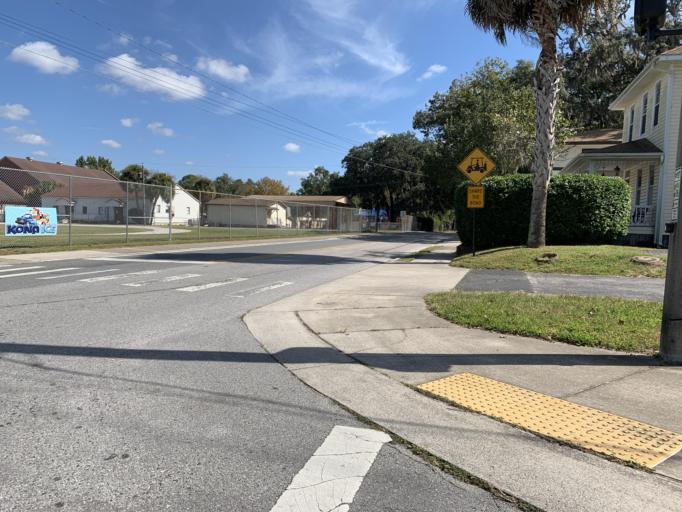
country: US
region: Florida
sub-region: Marion County
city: Ocala
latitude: 29.1804
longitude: -82.1342
